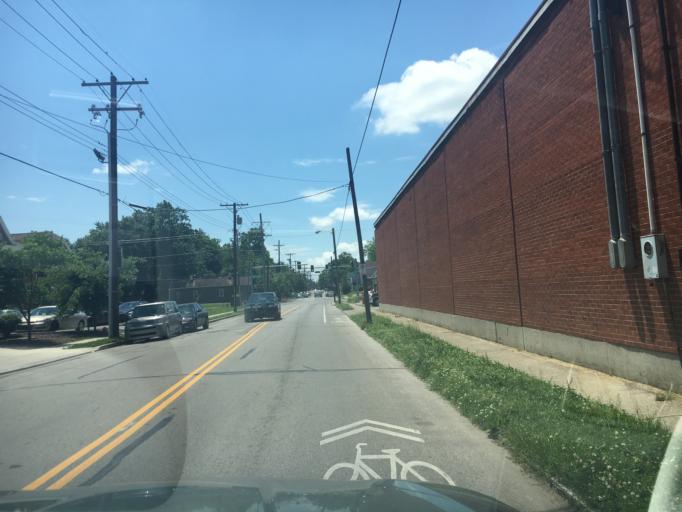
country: US
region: Kentucky
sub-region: Fayette County
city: Mount Vernon
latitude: 38.0572
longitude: -84.4957
